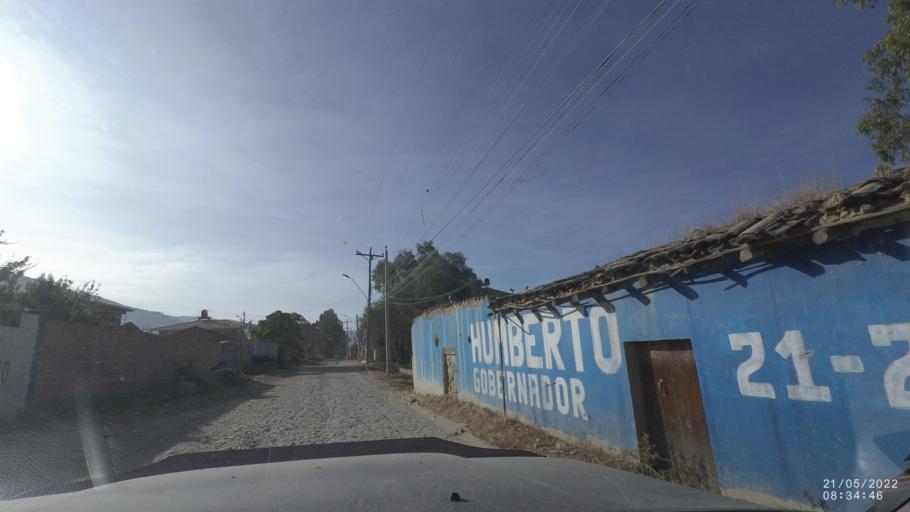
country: BO
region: Cochabamba
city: Cochabamba
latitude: -17.3875
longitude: -66.0453
